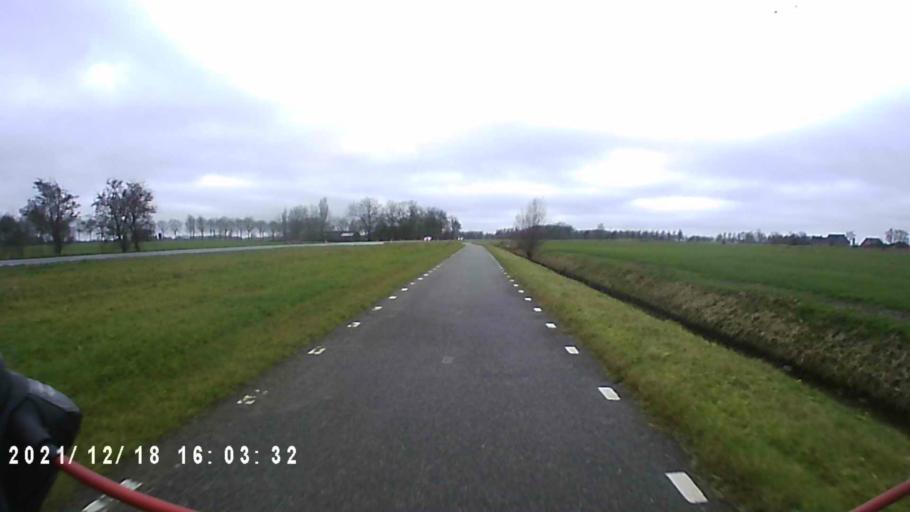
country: NL
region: Friesland
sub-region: Gemeente Dongeradeel
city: Anjum
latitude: 53.3499
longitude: 6.0805
